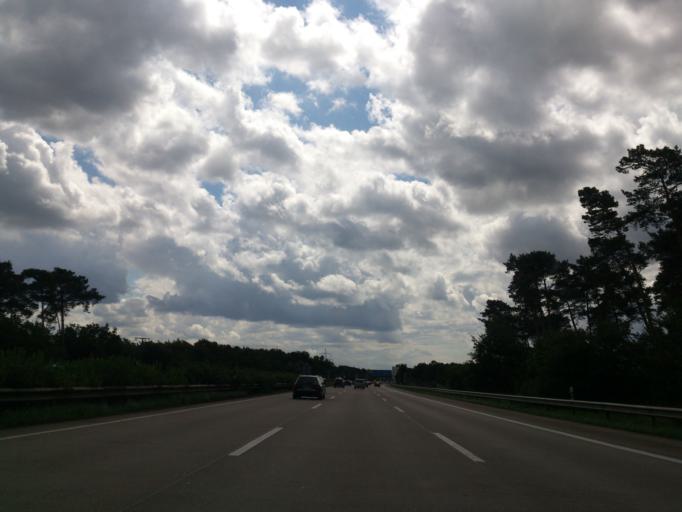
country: DE
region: Lower Saxony
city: Elze
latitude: 52.5681
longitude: 9.7838
